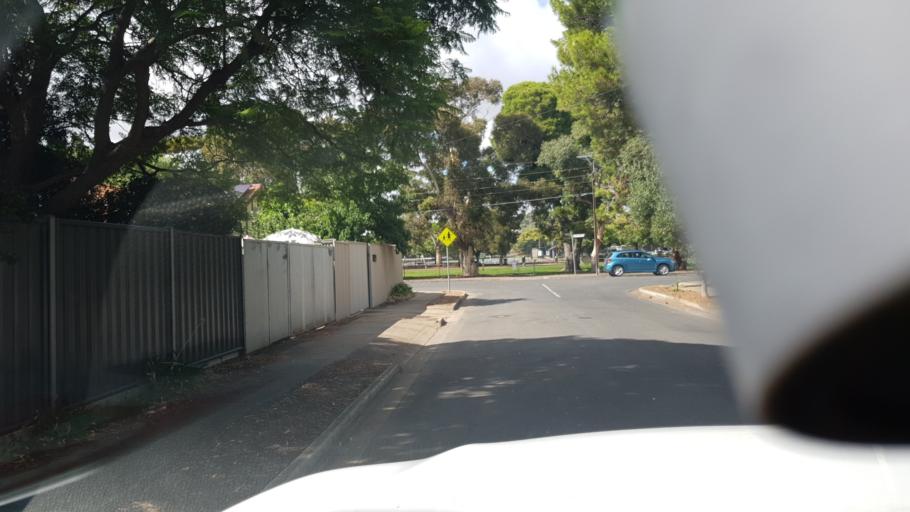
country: AU
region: South Australia
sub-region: Holdfast Bay
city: Seacliff Park
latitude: -35.0241
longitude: 138.5285
